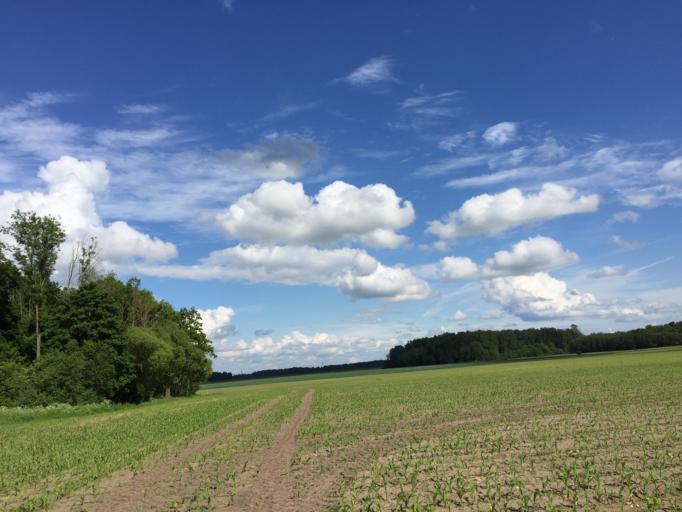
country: LV
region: Dobeles Rajons
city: Dobele
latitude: 56.6743
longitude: 23.3945
